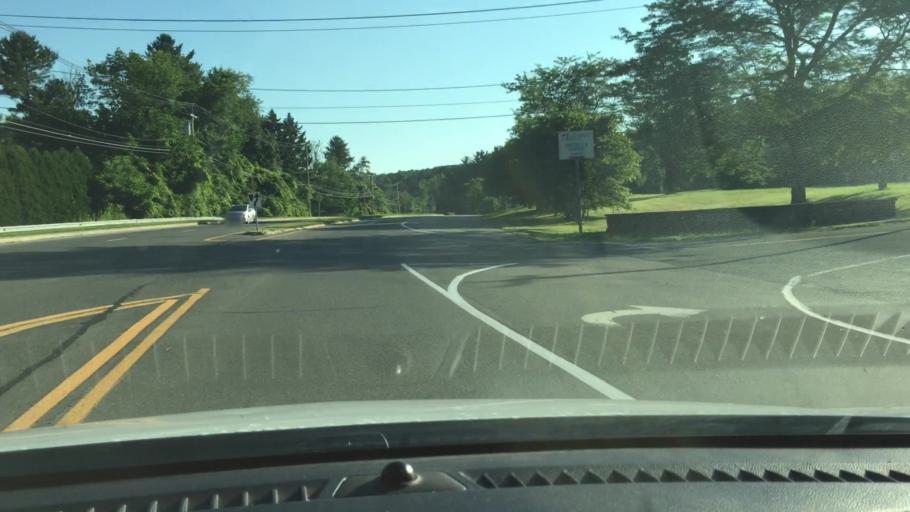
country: US
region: Massachusetts
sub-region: Berkshire County
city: Lenox
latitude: 42.3701
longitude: -73.2803
